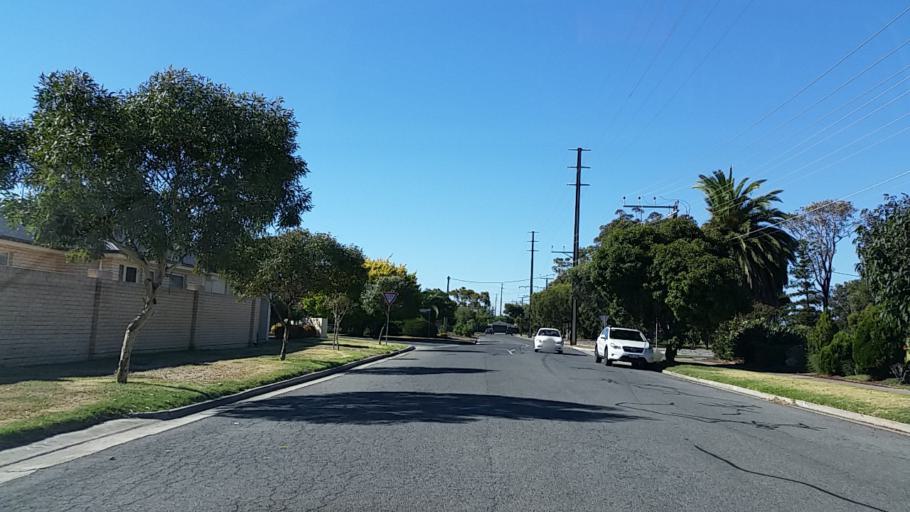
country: AU
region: South Australia
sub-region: Charles Sturt
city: Henley Beach
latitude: -34.9247
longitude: 138.5064
